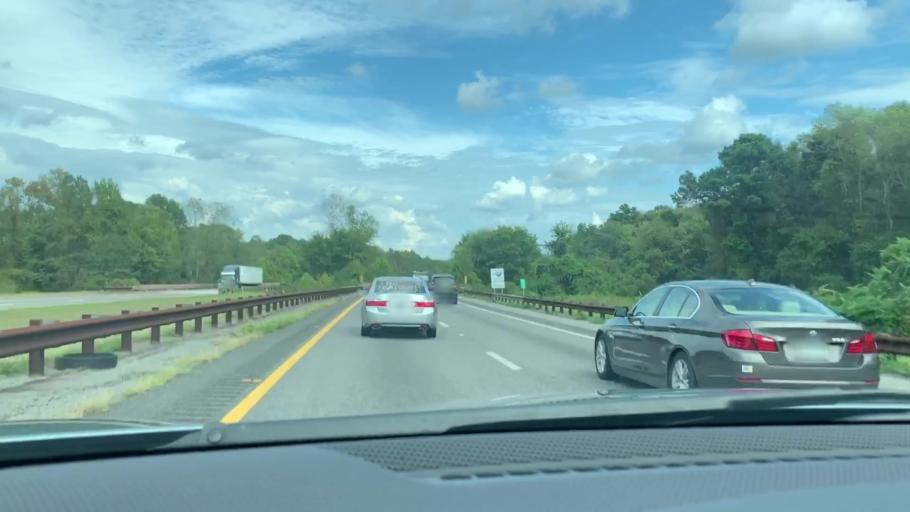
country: US
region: South Carolina
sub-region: Jasper County
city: Hardeeville
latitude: 32.2531
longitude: -81.1250
